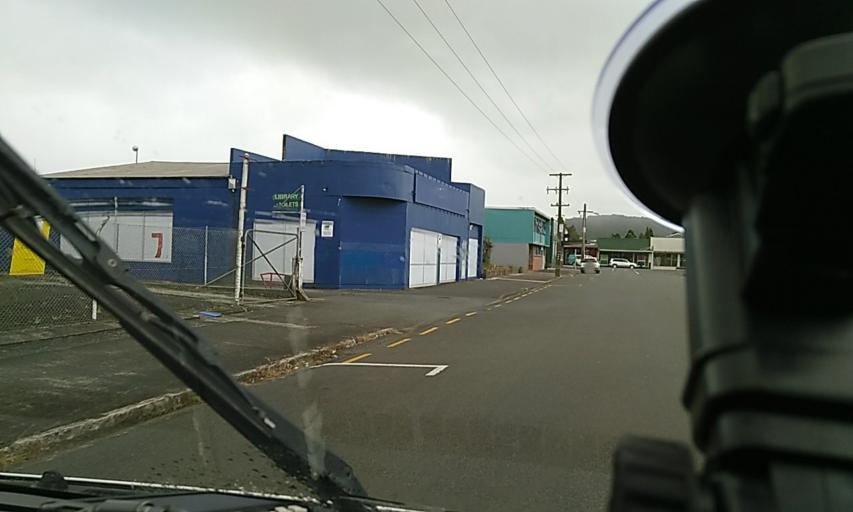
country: NZ
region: Northland
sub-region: Far North District
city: Waimate North
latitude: -35.4079
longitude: 173.8015
